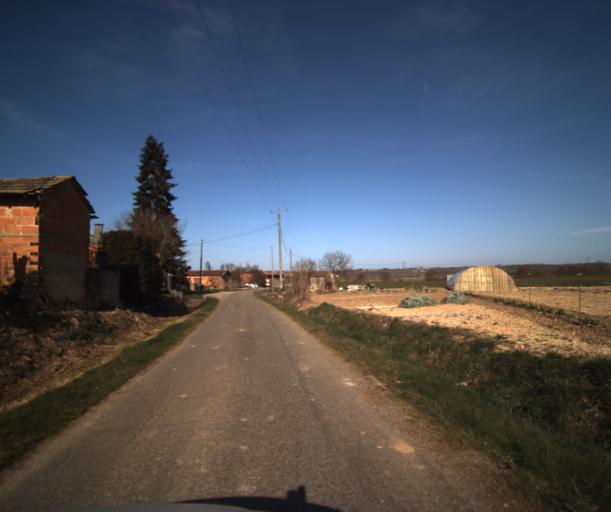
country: FR
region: Midi-Pyrenees
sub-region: Departement du Tarn-et-Garonne
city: Corbarieu
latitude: 43.9354
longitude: 1.3385
